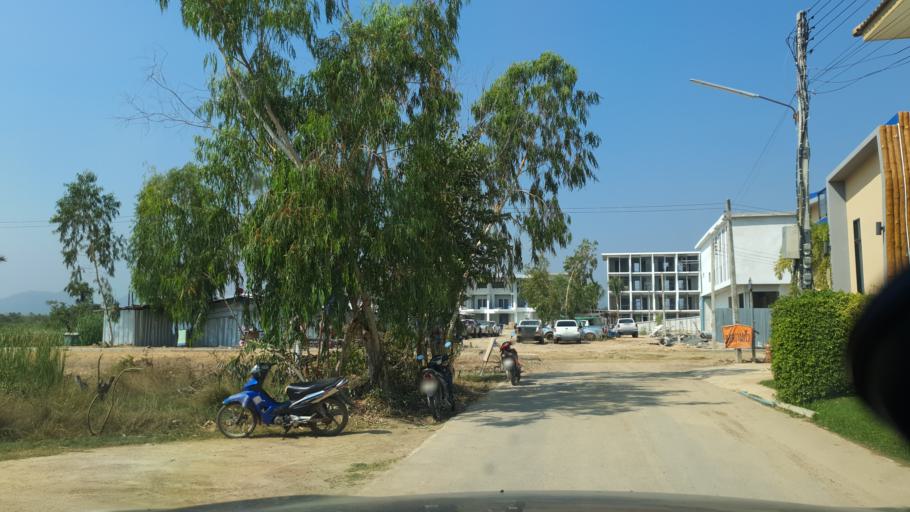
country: TH
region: Phetchaburi
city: Cha-am
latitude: 12.7838
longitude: 99.9753
